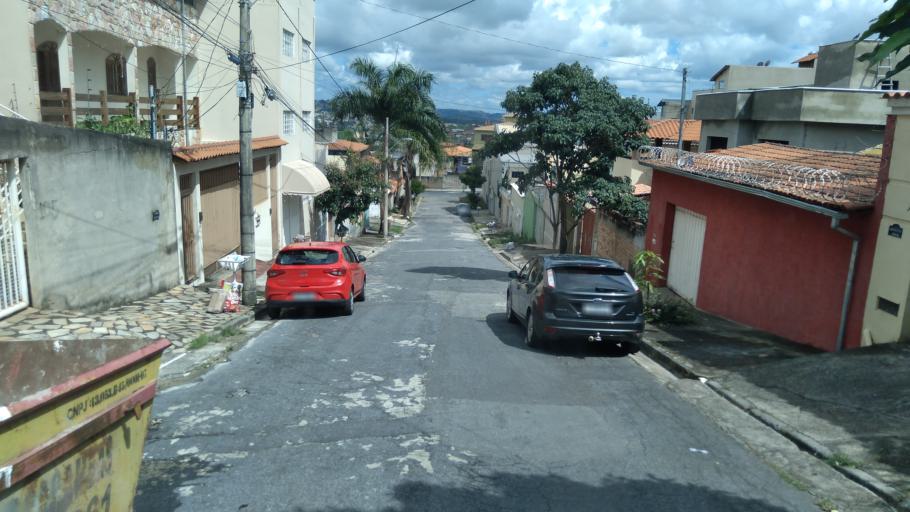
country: BR
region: Minas Gerais
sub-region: Belo Horizonte
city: Belo Horizonte
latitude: -19.8627
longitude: -43.8870
